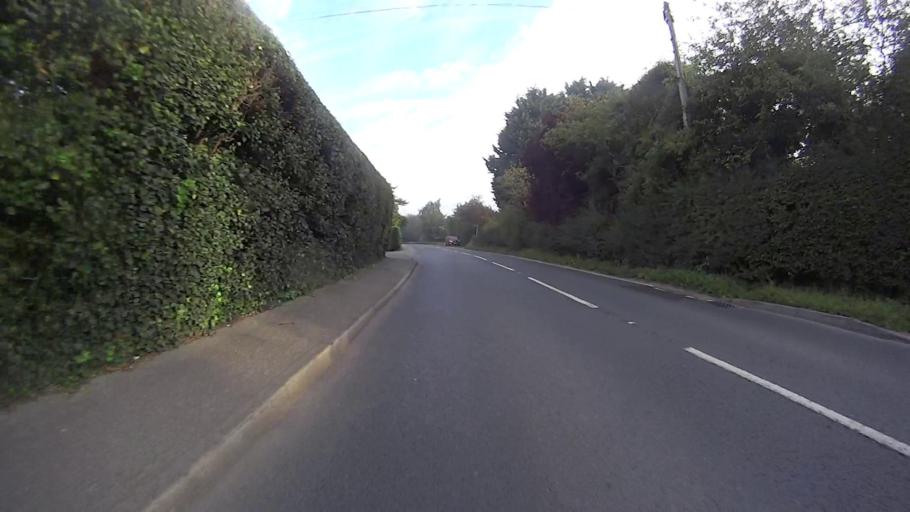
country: GB
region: England
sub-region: West Sussex
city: Copthorne
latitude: 51.1543
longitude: -0.1112
